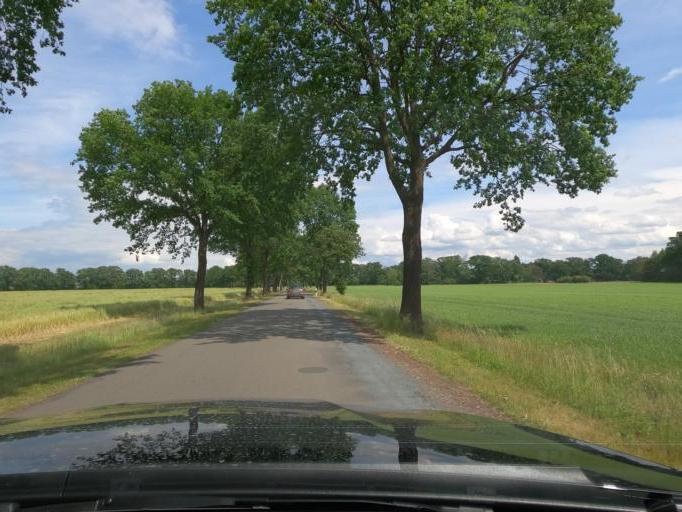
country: DE
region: Lower Saxony
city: Lindwedel
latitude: 52.6177
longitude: 9.6449
